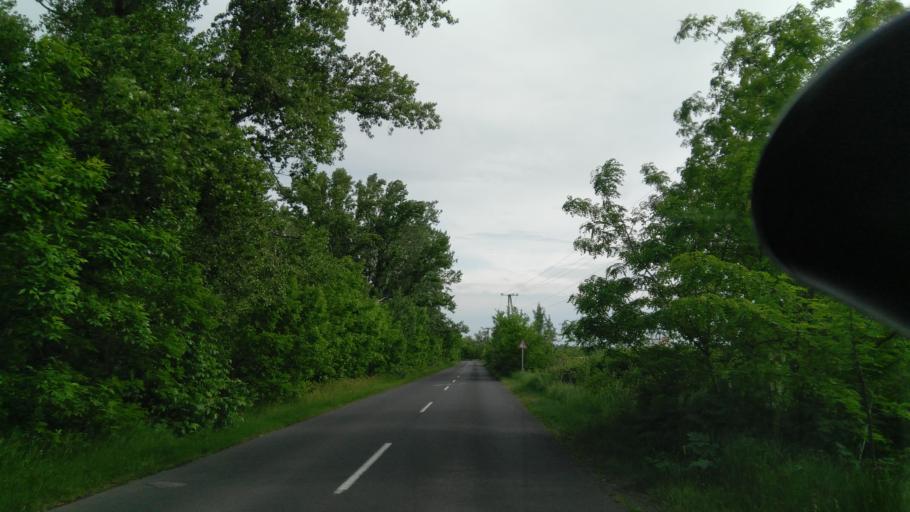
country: HU
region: Bekes
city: Oroshaza
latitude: 46.5944
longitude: 20.6830
